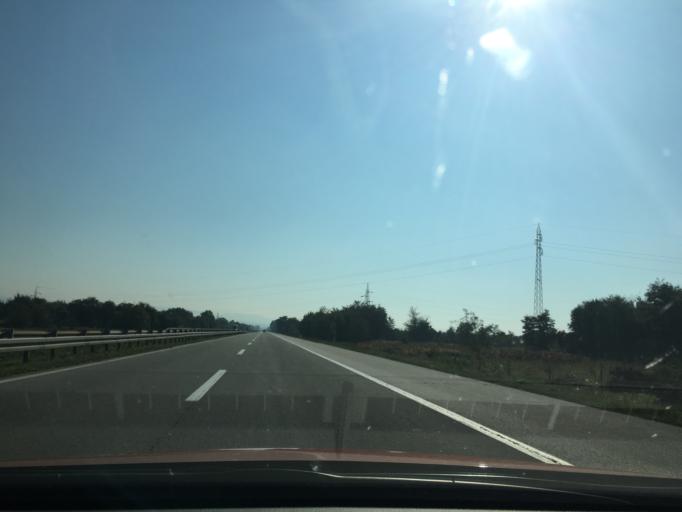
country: RS
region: Central Serbia
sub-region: Pomoravski Okrug
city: Jagodina
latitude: 43.9670
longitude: 21.3128
